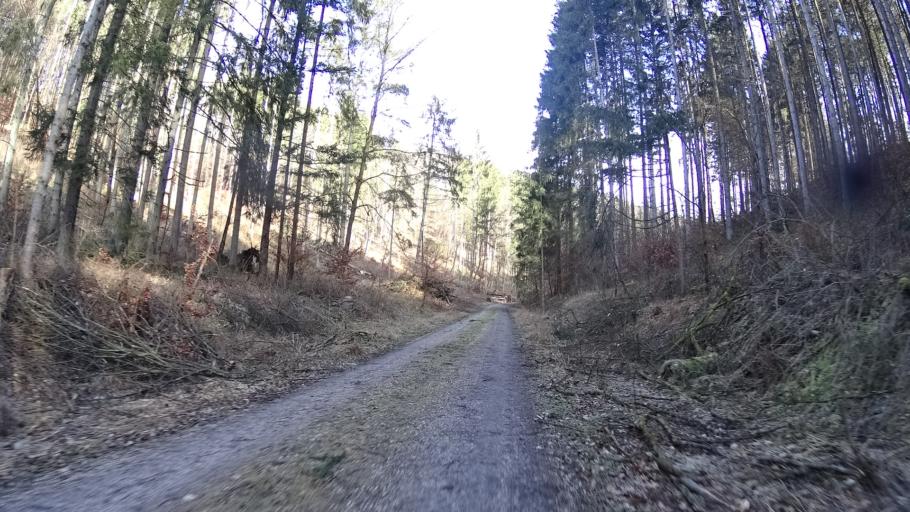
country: DE
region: Bavaria
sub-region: Upper Bavaria
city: Walting
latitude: 48.9009
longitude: 11.3032
